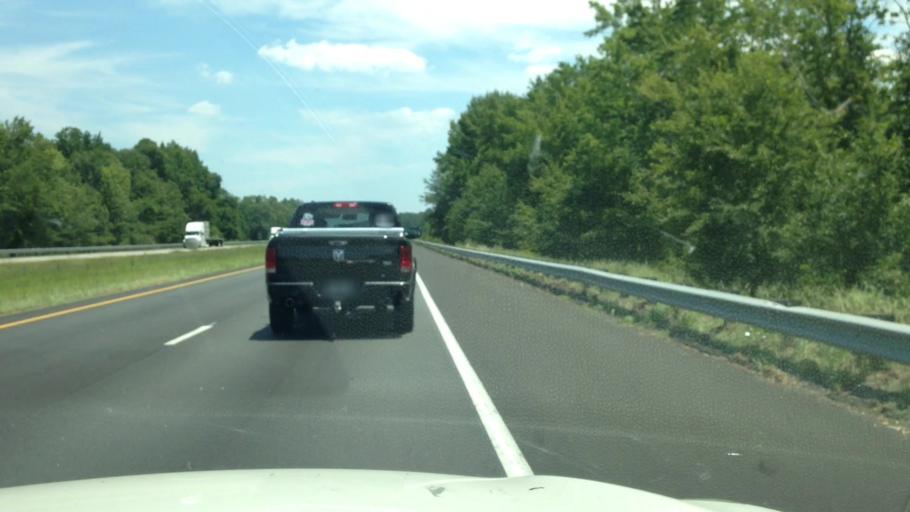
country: US
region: South Carolina
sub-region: Lee County
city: Bishopville
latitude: 34.1883
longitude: -80.1811
